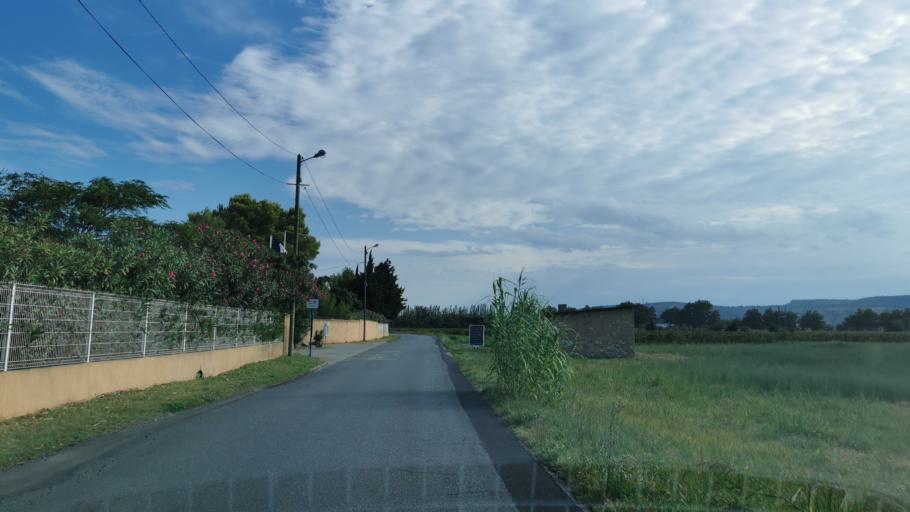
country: FR
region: Languedoc-Roussillon
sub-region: Departement de l'Aude
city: Narbonne
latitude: 43.1360
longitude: 3.0256
